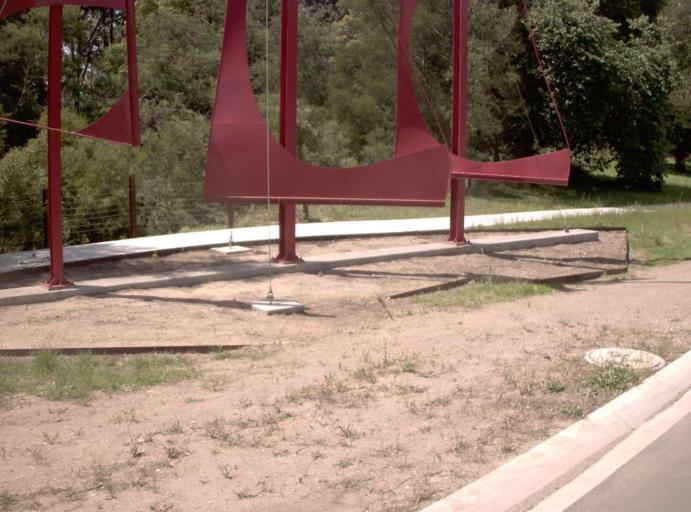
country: AU
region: Victoria
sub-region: Wellington
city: Sale
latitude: -38.1123
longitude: 147.0563
